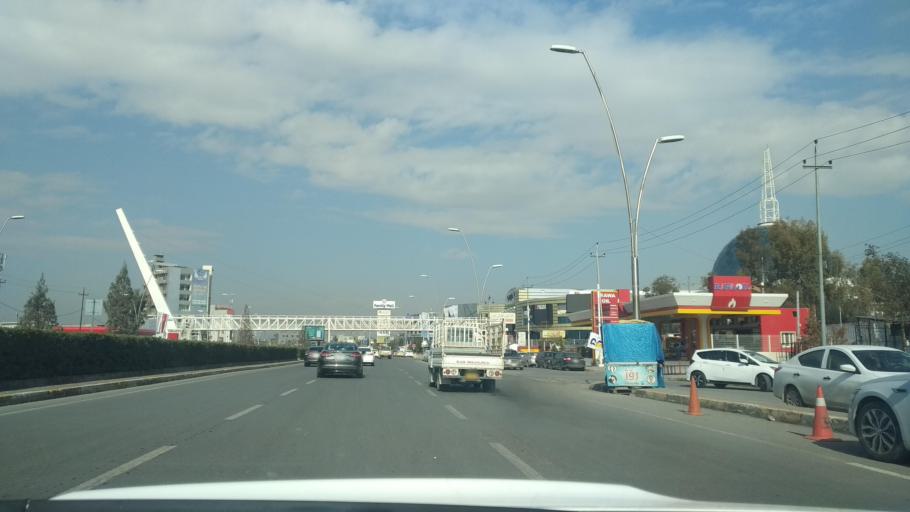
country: IQ
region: Arbil
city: Erbil
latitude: 36.2078
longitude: 44.0446
